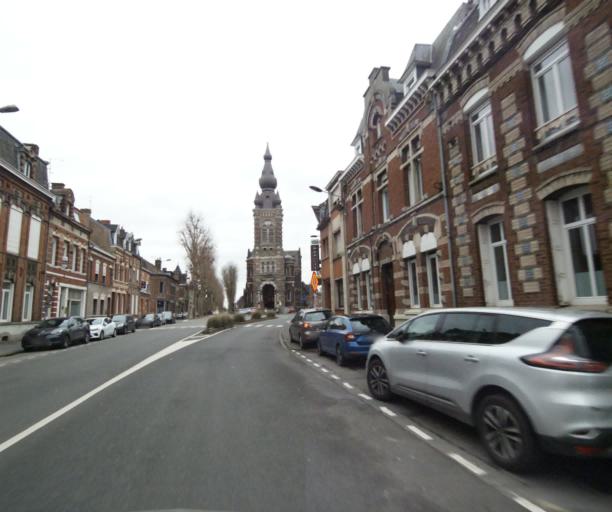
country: FR
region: Nord-Pas-de-Calais
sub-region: Departement du Nord
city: Valenciennes
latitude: 50.3622
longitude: 3.5323
